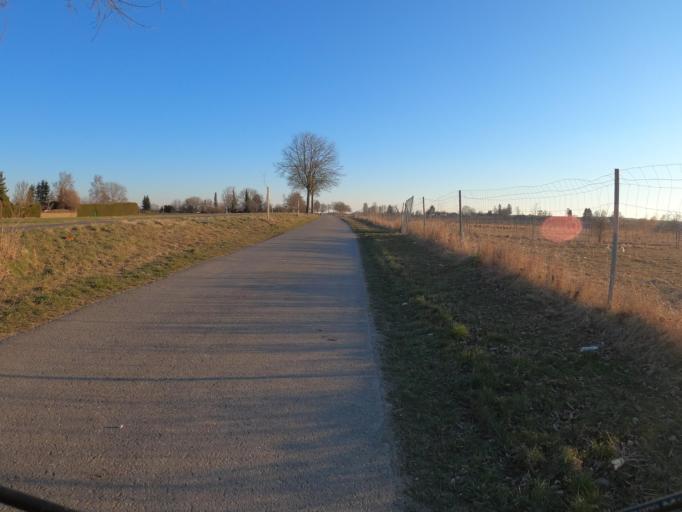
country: DE
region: Baden-Wuerttemberg
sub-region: Tuebingen Region
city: Langenau
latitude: 48.4844
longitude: 10.1153
